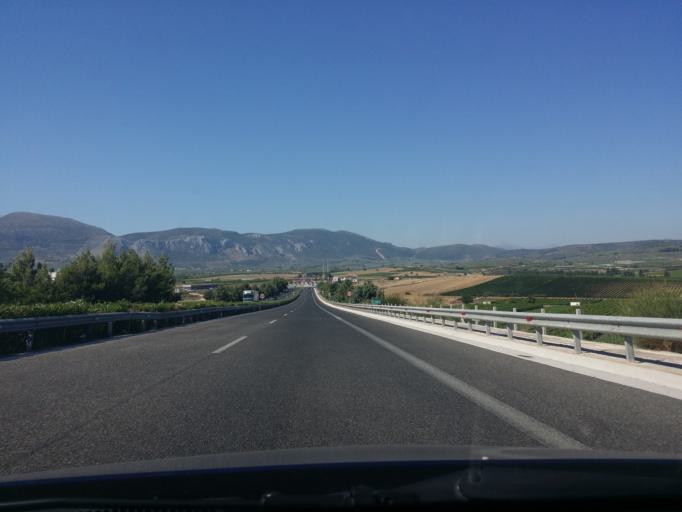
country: GR
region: Peloponnese
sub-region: Nomos Korinthias
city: Ayios Vasilios
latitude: 37.8426
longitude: 22.8126
